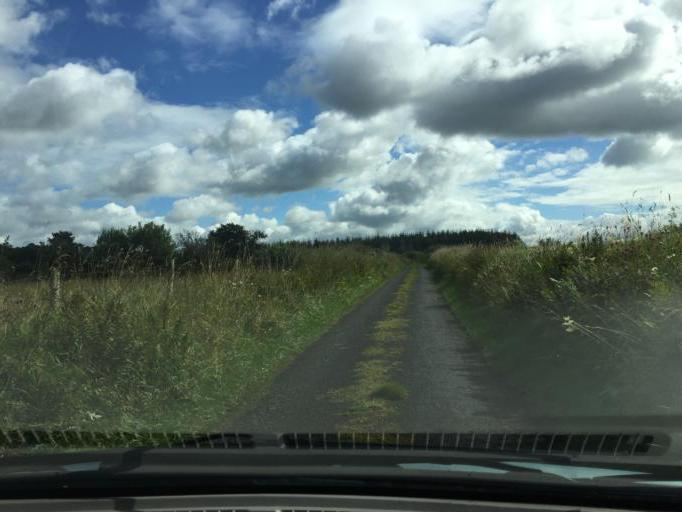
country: IE
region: Connaught
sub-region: Maigh Eo
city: Swinford
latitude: 54.0325
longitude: -8.8999
